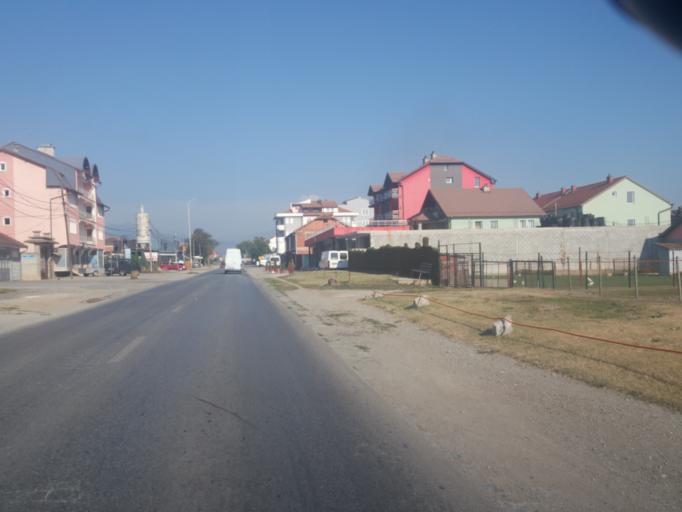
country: XK
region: Gjakova
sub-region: Komuna e Gjakoves
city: Gjakove
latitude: 42.4031
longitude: 20.4126
